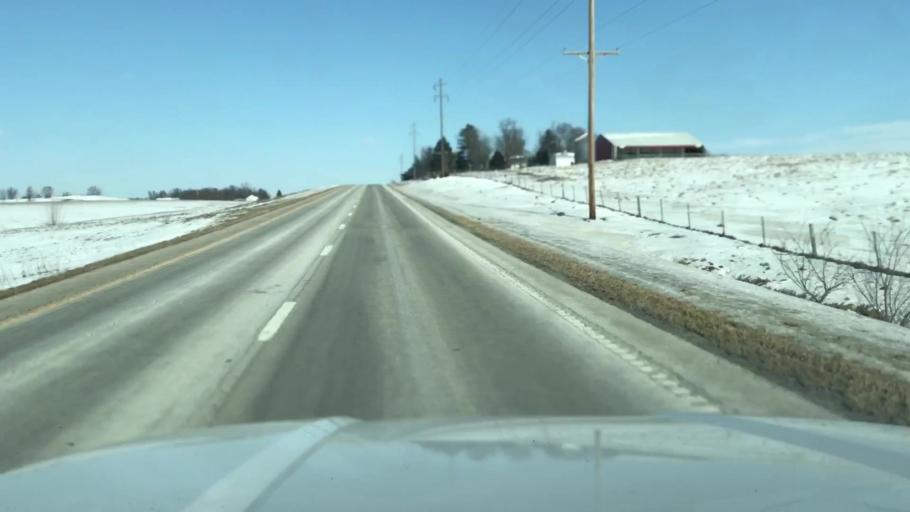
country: US
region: Missouri
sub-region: Nodaway County
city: Maryville
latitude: 40.1502
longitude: -94.8691
